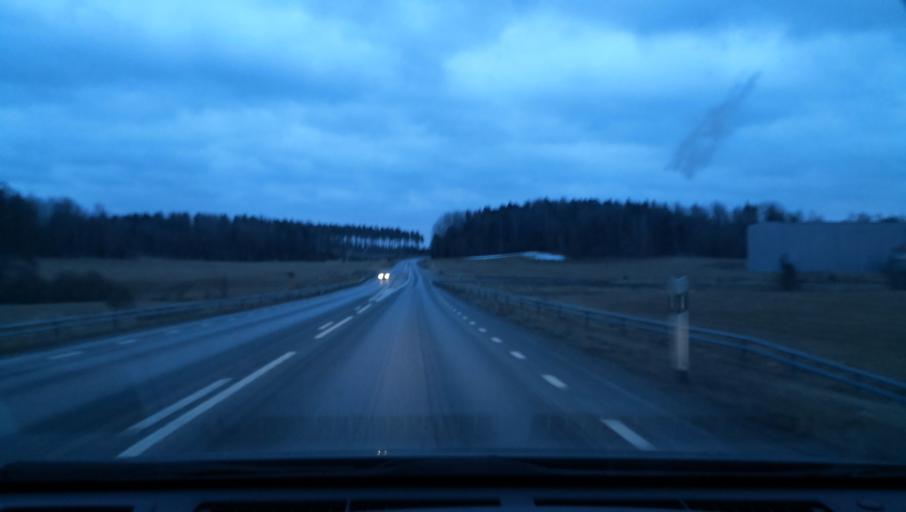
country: SE
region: Vaestmanland
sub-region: Kopings Kommun
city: Kolsva
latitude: 59.5813
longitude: 15.8727
